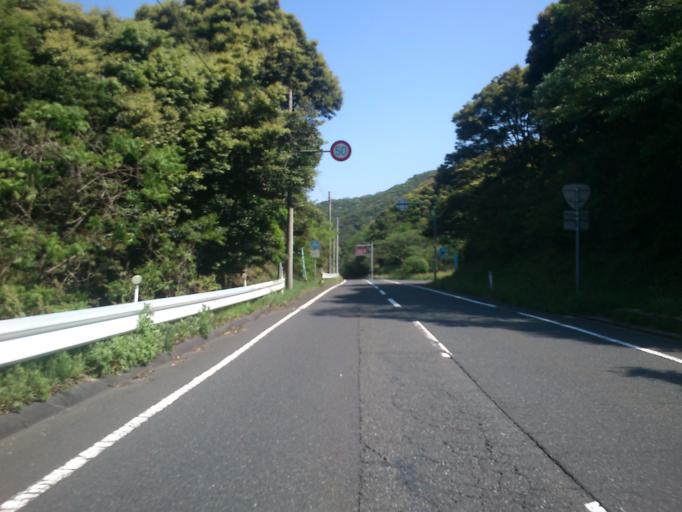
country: JP
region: Kyoto
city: Miyazu
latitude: 35.7066
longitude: 135.0692
